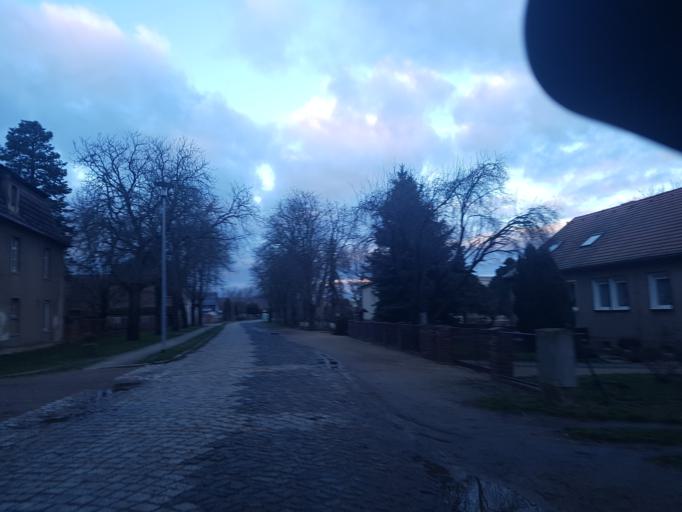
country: DE
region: Brandenburg
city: Muhlberg
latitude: 51.4727
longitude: 13.2042
